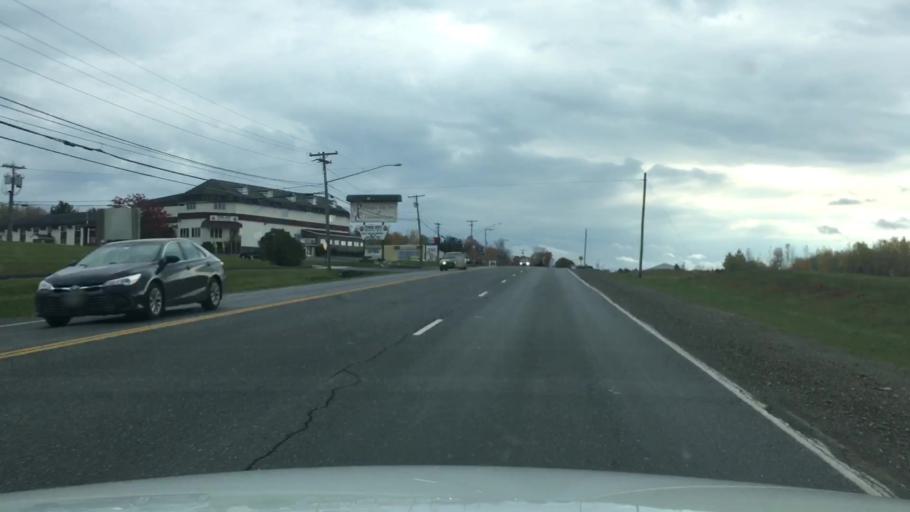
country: US
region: Maine
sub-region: Aroostook County
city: Presque Isle
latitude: 46.6686
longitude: -68.0126
